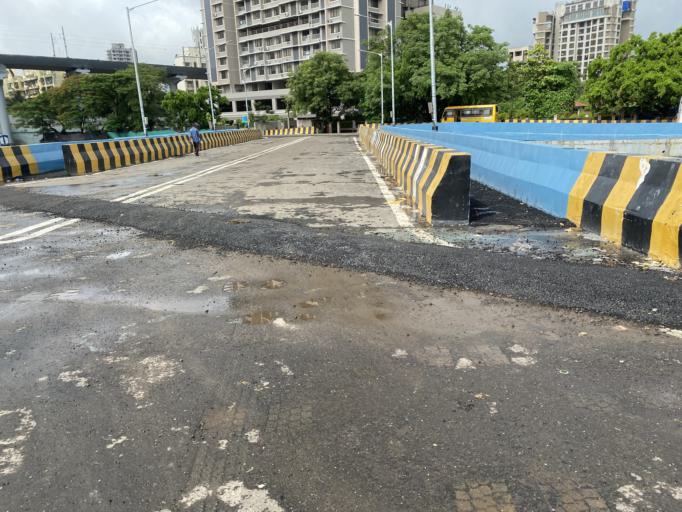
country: IN
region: Maharashtra
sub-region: Mumbai Suburban
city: Borivli
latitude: 19.2600
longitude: 72.8555
